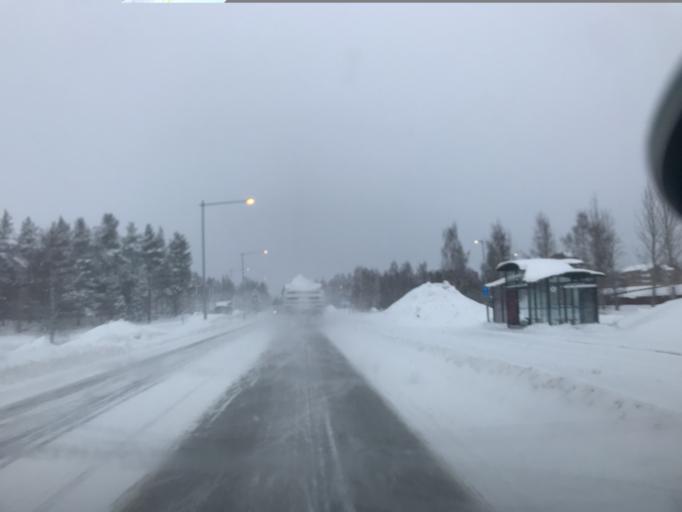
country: SE
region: Norrbotten
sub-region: Lulea Kommun
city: Lulea
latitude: 65.6165
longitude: 22.1315
